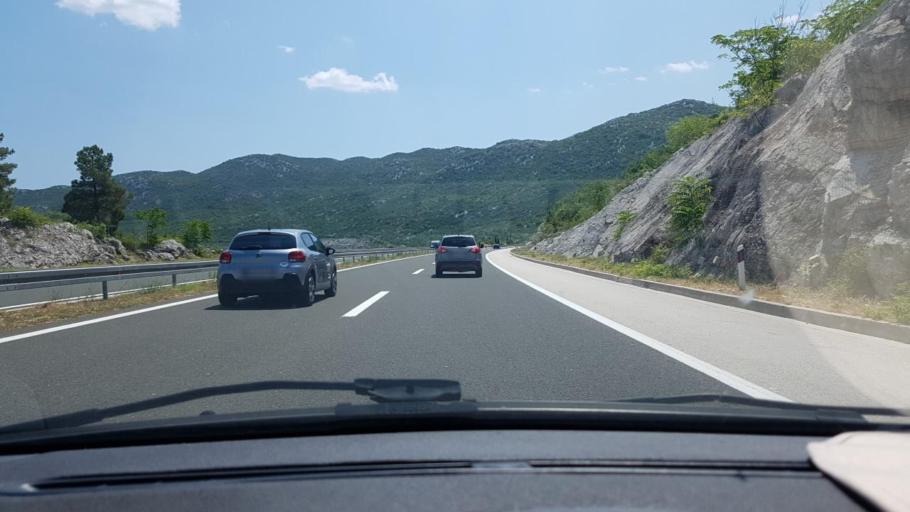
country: HR
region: Splitsko-Dalmatinska
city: Runovic
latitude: 43.2381
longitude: 17.2351
